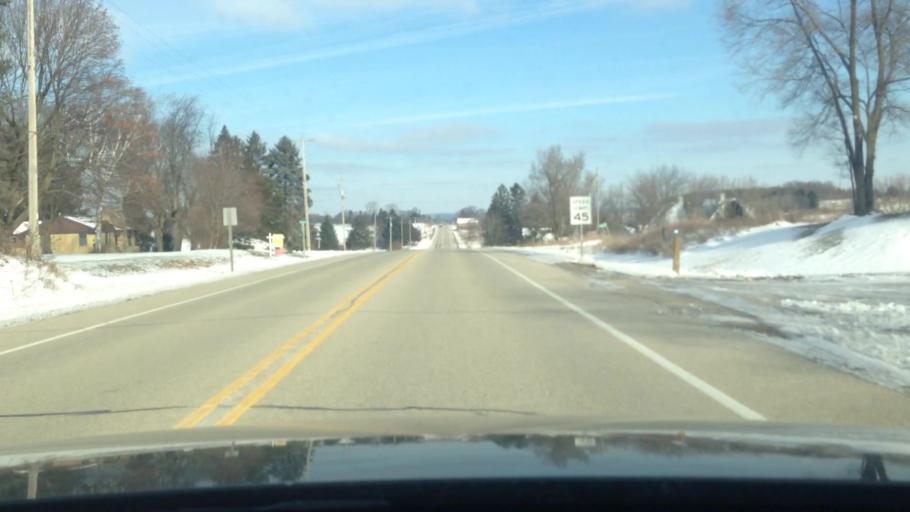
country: US
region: Wisconsin
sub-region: Walworth County
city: East Troy
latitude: 42.7589
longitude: -88.4066
